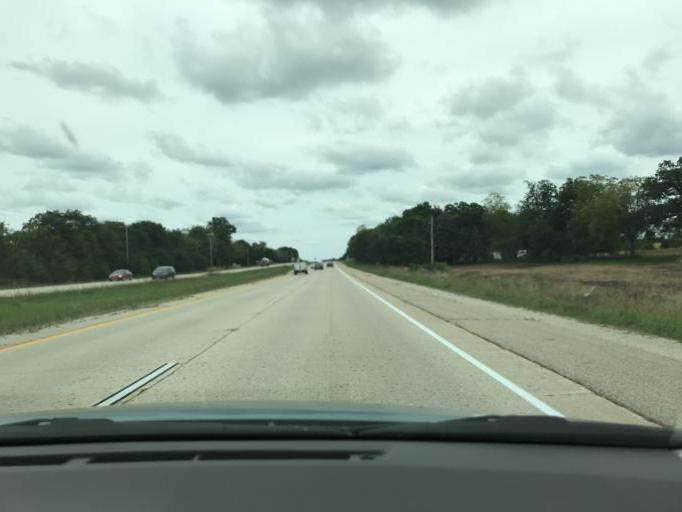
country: US
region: Wisconsin
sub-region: Kenosha County
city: Paddock Lake
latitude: 42.5680
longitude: -88.0830
